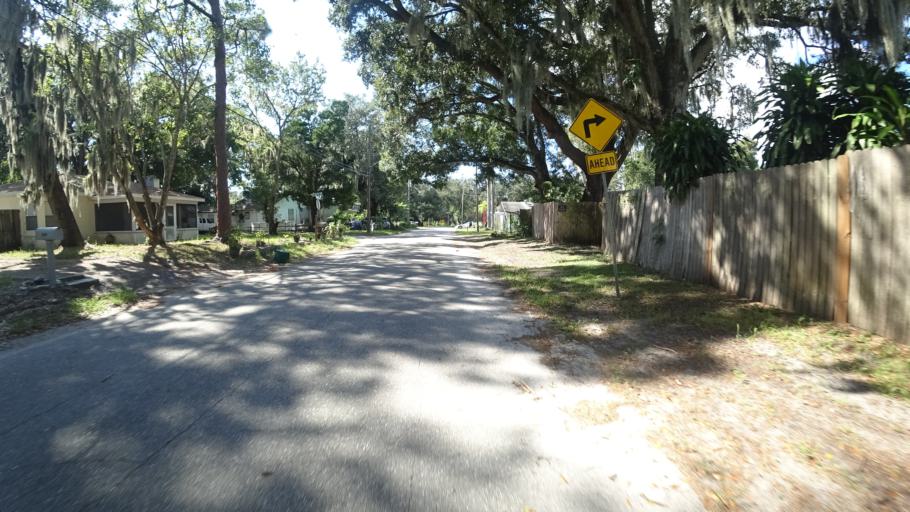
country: US
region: Florida
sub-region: Manatee County
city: Bradenton
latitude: 27.4833
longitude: -82.5777
